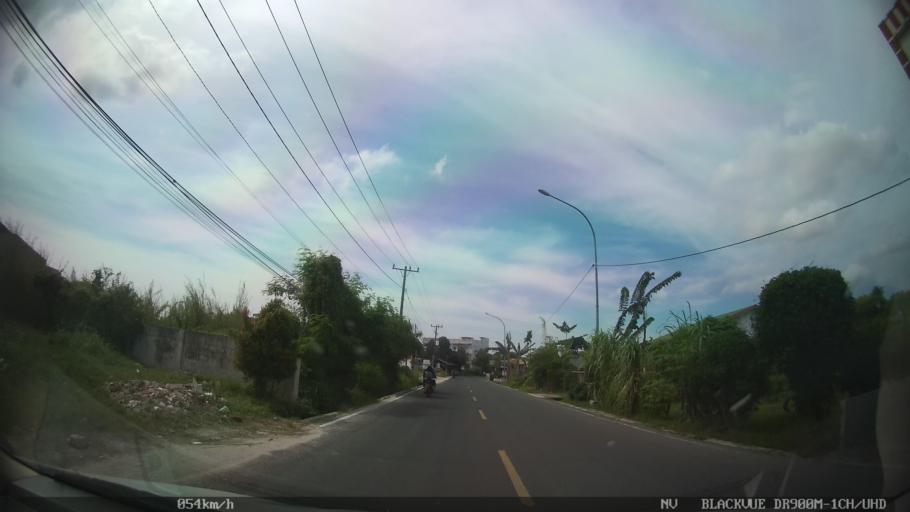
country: ID
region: North Sumatra
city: Percut
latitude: 3.5905
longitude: 98.8587
